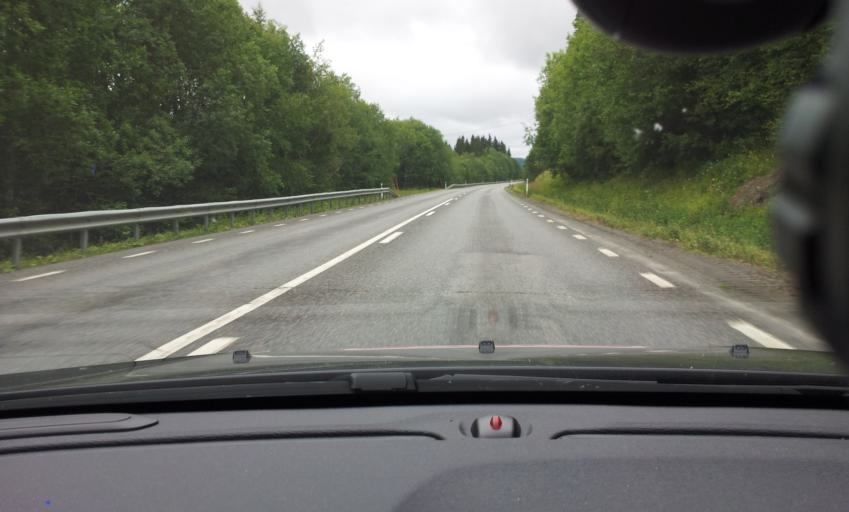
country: SE
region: Jaemtland
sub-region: Are Kommun
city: Are
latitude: 63.3980
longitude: 12.9705
